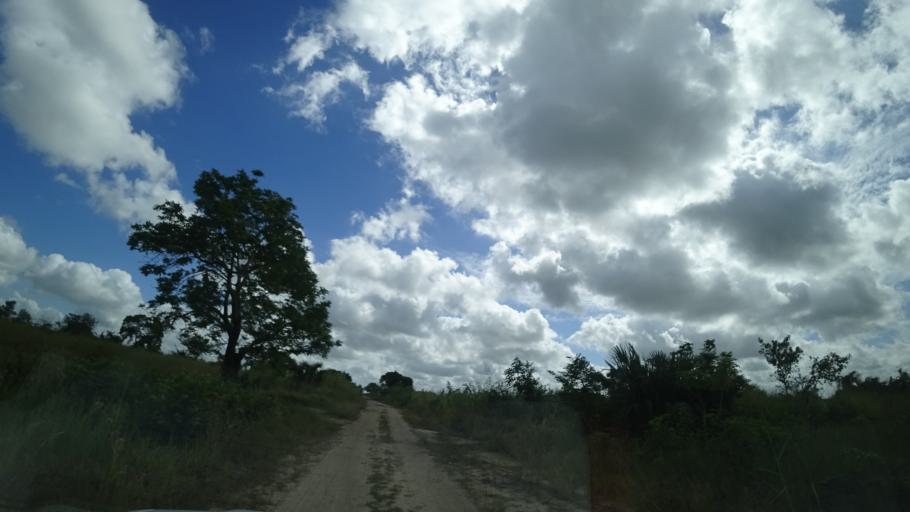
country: MZ
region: Sofala
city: Dondo
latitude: -19.3839
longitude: 34.5926
